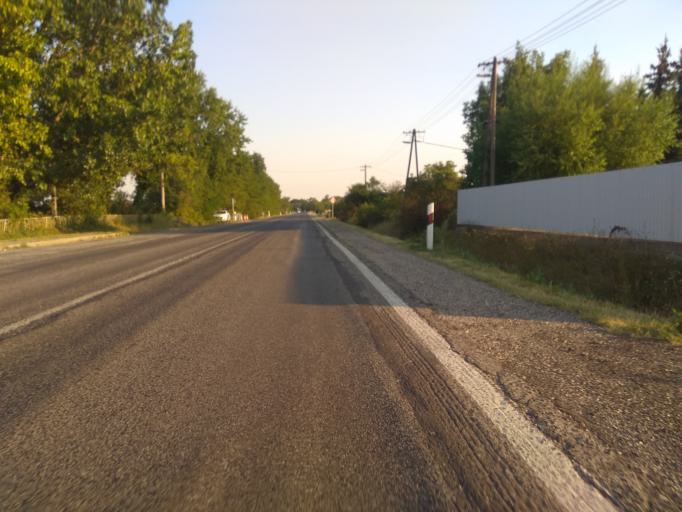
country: HU
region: Borsod-Abauj-Zemplen
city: Nyekladhaza
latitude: 47.9734
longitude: 20.8303
